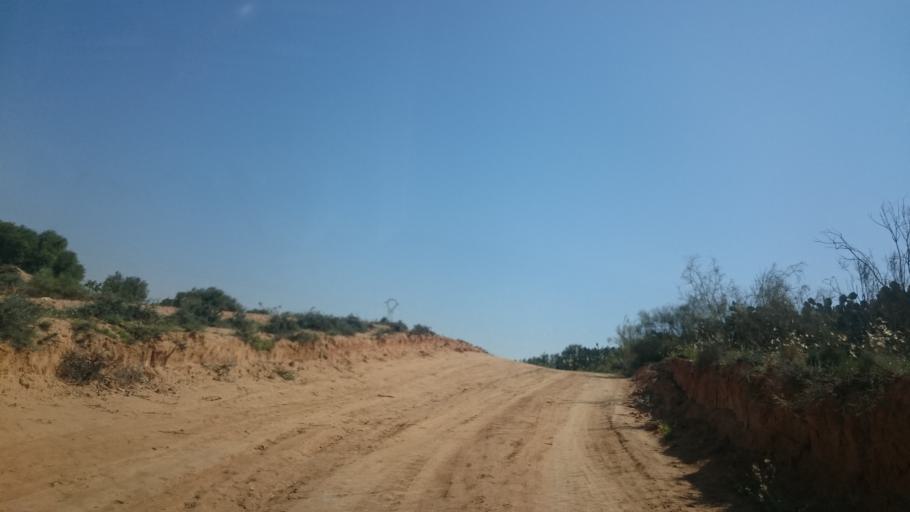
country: TN
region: Safaqis
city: Sfax
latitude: 34.7879
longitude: 10.5385
